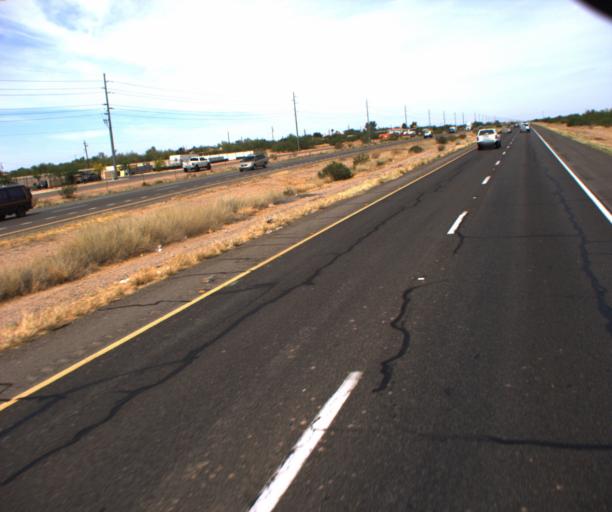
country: US
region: Arizona
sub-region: Maricopa County
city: Sun City West
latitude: 33.7059
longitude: -112.4362
